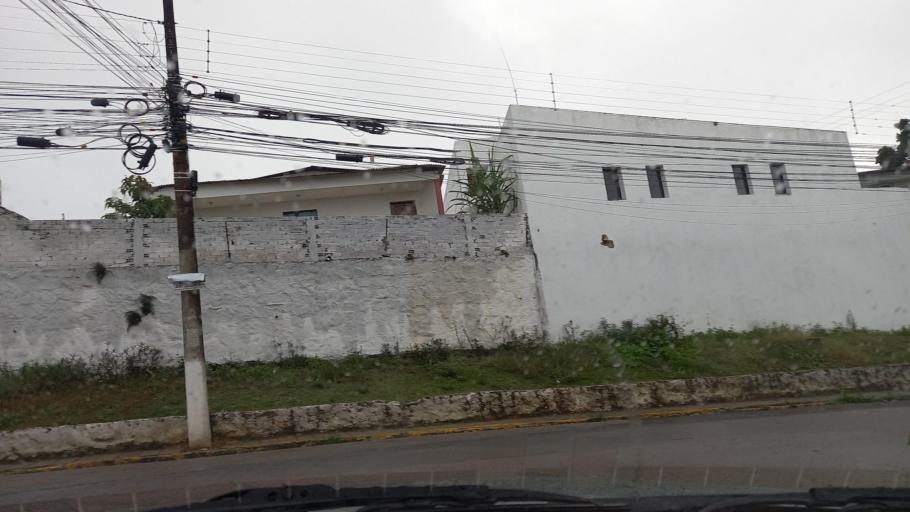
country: BR
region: Pernambuco
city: Garanhuns
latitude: -8.8868
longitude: -36.4991
